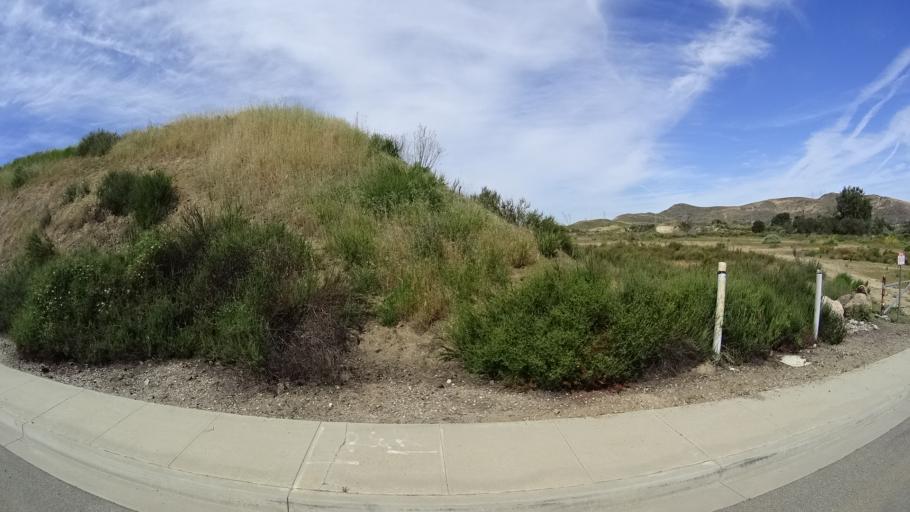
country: US
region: California
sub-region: Ventura County
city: Casa Conejo
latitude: 34.2020
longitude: -118.9349
